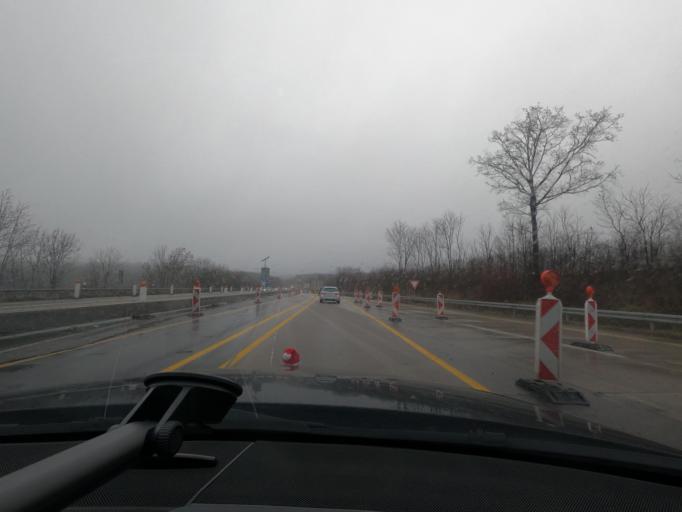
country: DE
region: Lower Saxony
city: Holle
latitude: 52.1091
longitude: 10.1361
